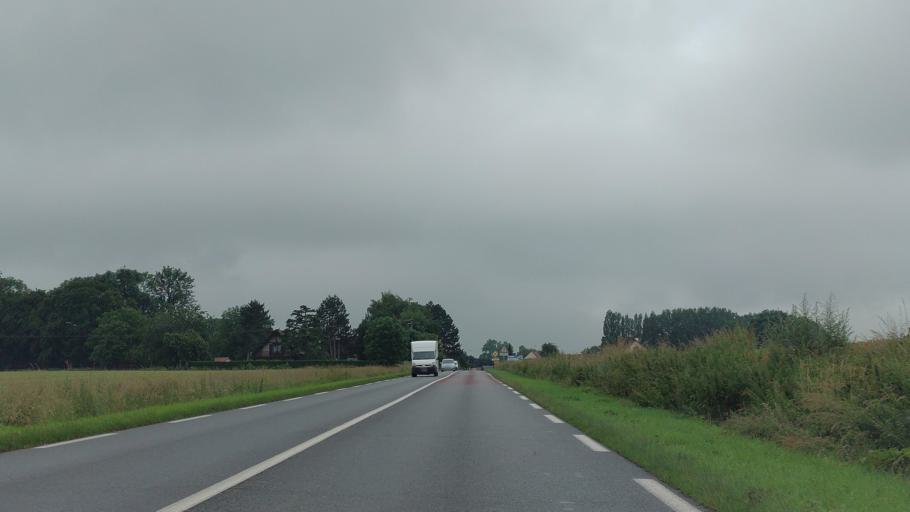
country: FR
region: Picardie
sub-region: Departement de la Somme
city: Chepy
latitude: 50.0810
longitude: 1.6327
